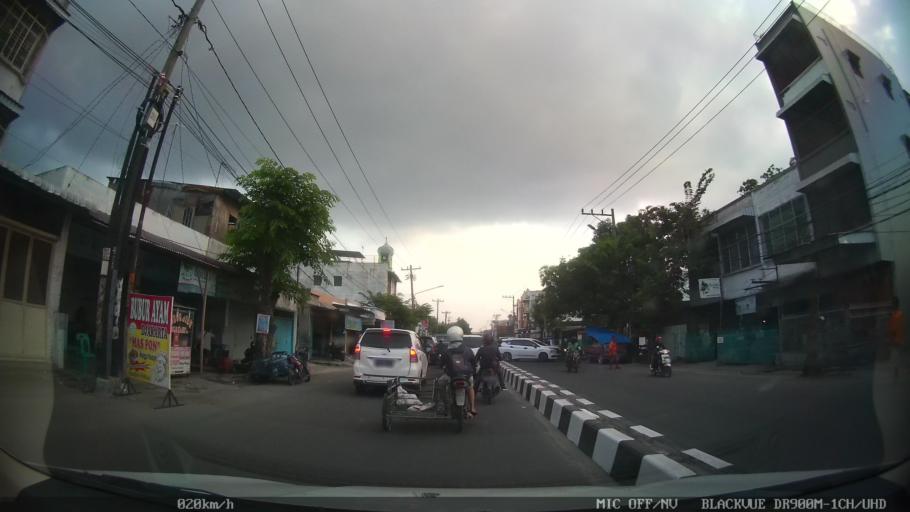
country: ID
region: North Sumatra
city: Medan
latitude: 3.5926
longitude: 98.7115
